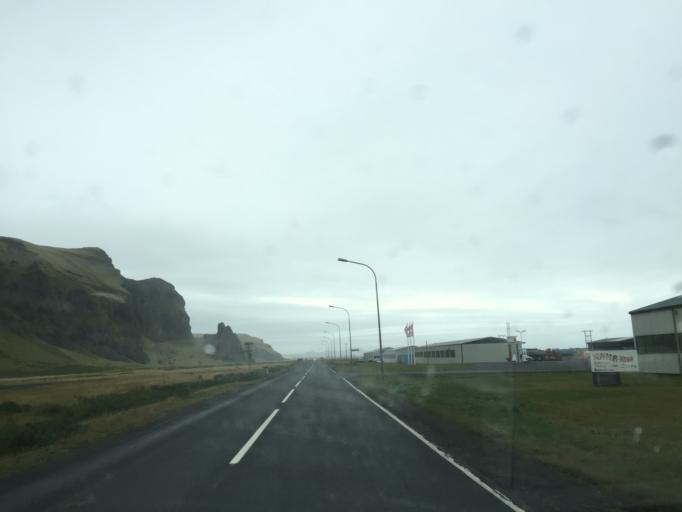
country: IS
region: South
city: Vestmannaeyjar
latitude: 63.4177
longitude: -18.9957
